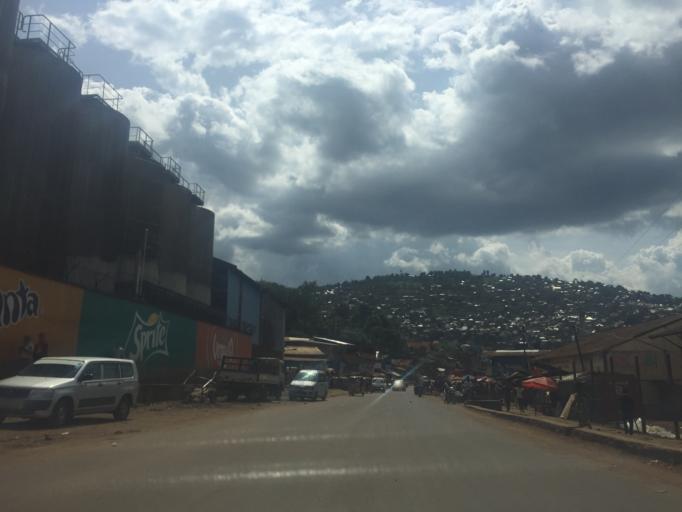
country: CD
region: South Kivu
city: Bukavu
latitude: -2.4840
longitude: 28.8433
